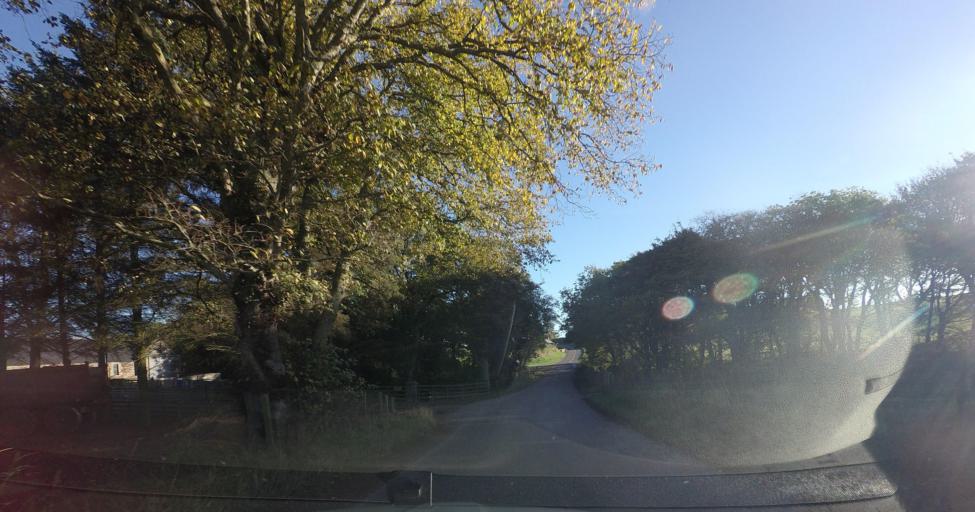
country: GB
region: Scotland
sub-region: Aberdeenshire
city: Rosehearty
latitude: 57.6765
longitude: -2.2911
